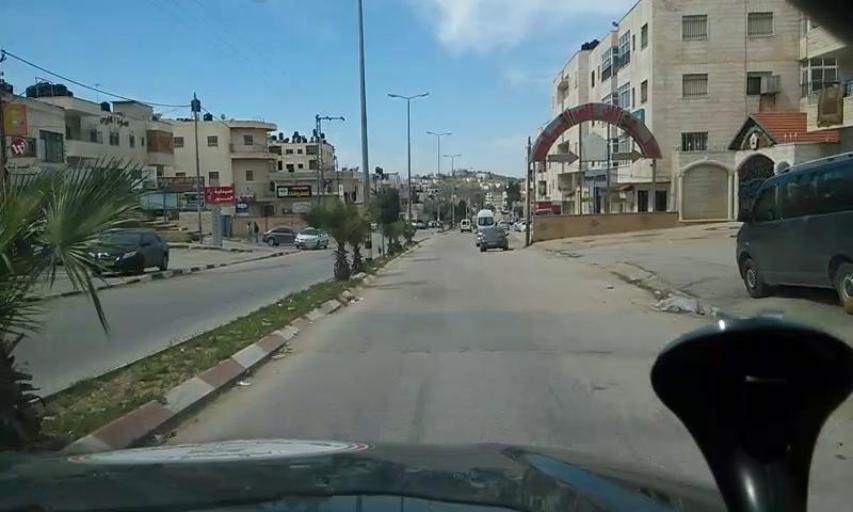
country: PS
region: West Bank
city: Bir Nabala
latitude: 31.8517
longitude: 35.2006
